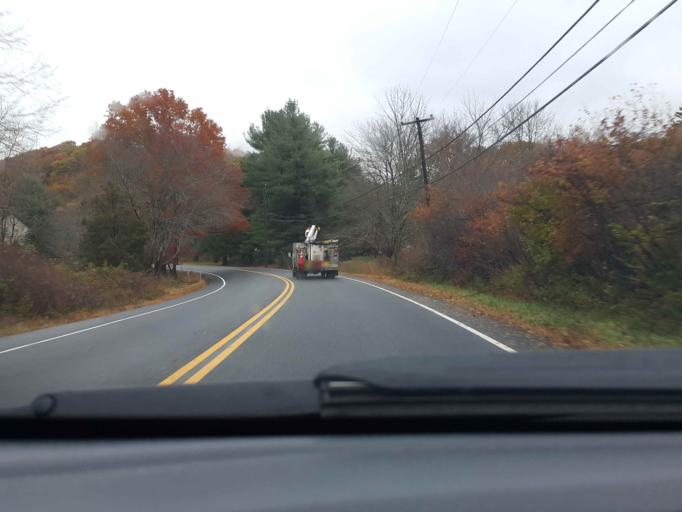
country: US
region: Connecticut
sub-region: Middlesex County
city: Durham
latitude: 41.4178
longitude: -72.6898
